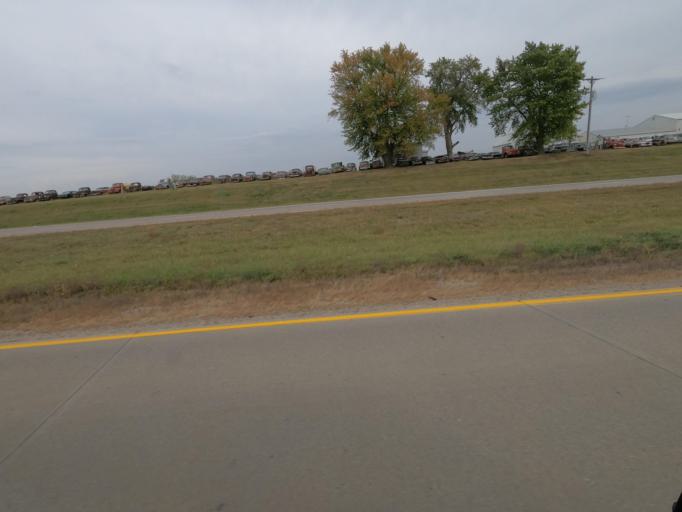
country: US
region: Iowa
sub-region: Marion County
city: Pella
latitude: 41.3882
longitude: -92.8321
